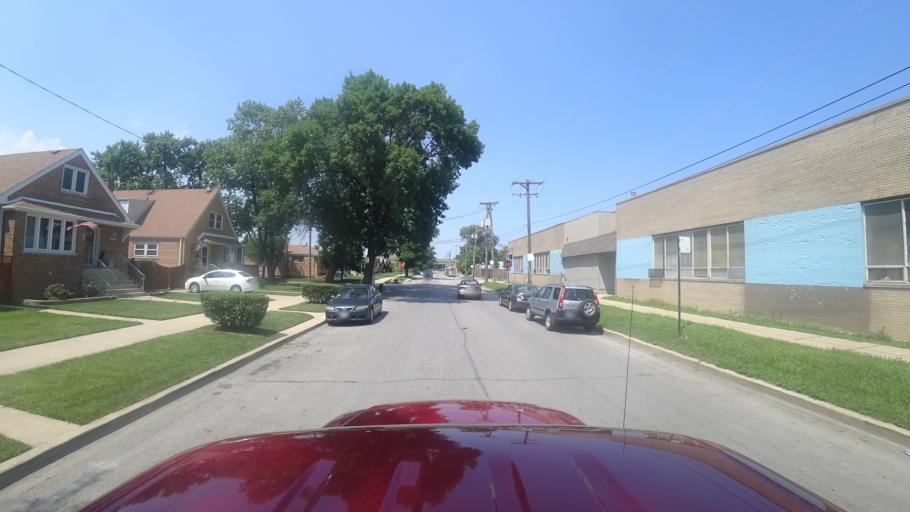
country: US
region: Illinois
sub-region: Cook County
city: Cicero
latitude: 41.7964
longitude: -87.7281
